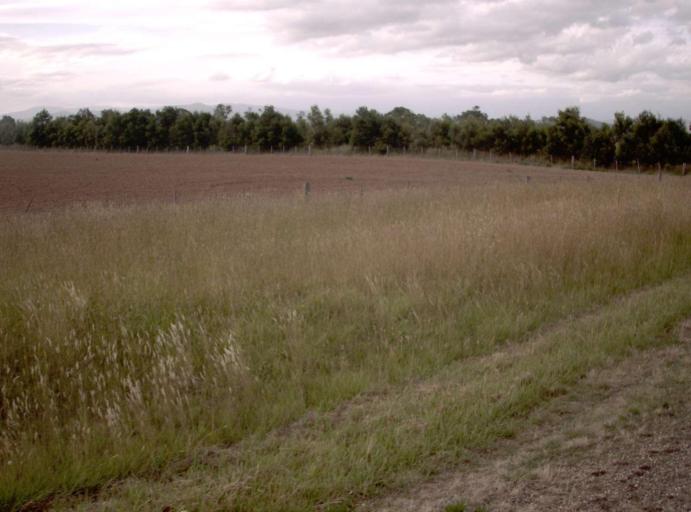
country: AU
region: Victoria
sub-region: Wellington
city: Sale
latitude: -37.8497
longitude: 147.0542
